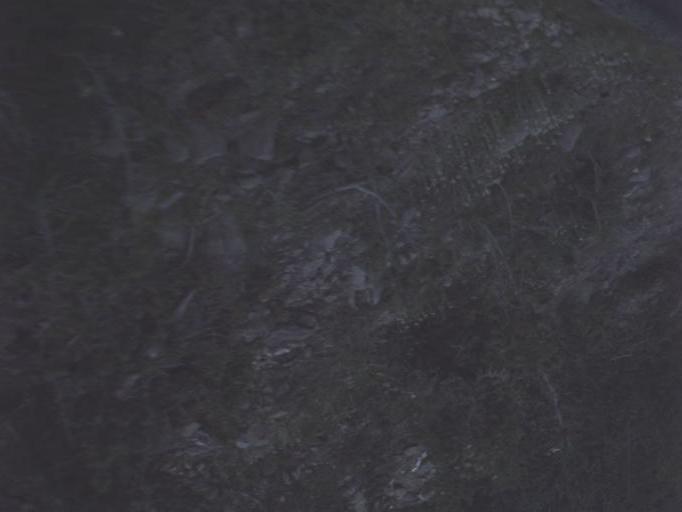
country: US
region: Utah
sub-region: Summit County
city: Kamas
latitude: 40.7482
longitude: -110.8751
